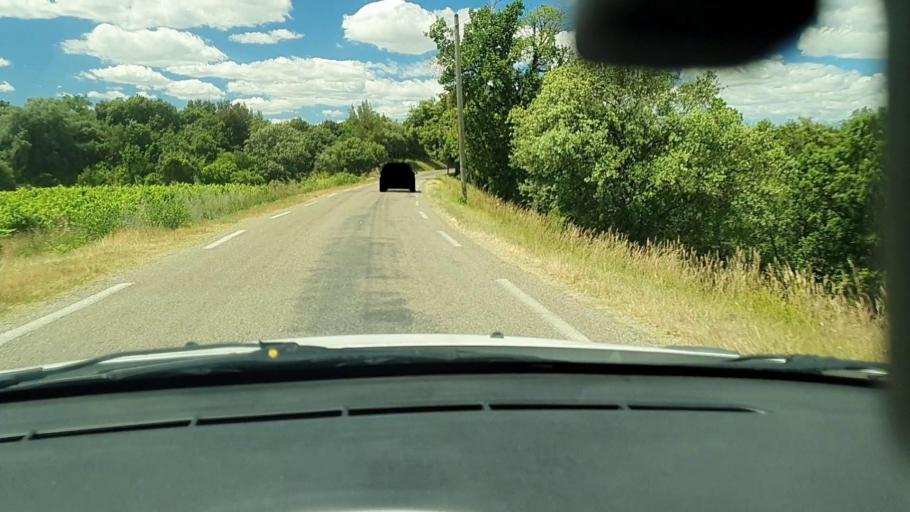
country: FR
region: Languedoc-Roussillon
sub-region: Departement du Gard
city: Cabrieres
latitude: 43.9544
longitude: 4.4567
